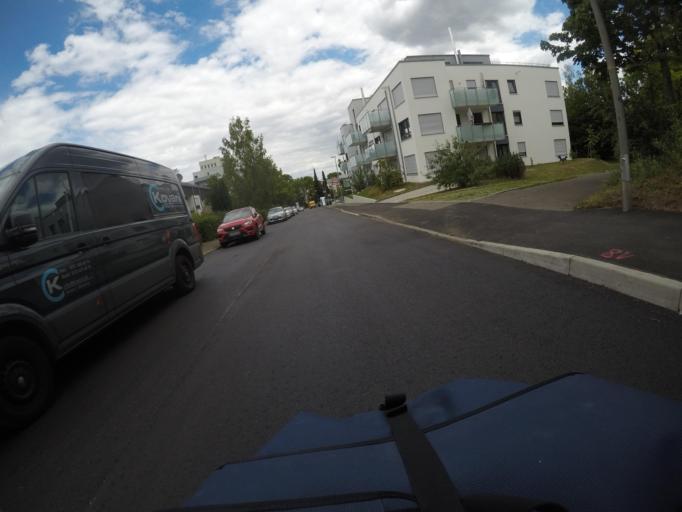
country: DE
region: Baden-Wuerttemberg
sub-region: Regierungsbezirk Stuttgart
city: Stuttgart Feuerbach
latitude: 48.8063
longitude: 9.1458
